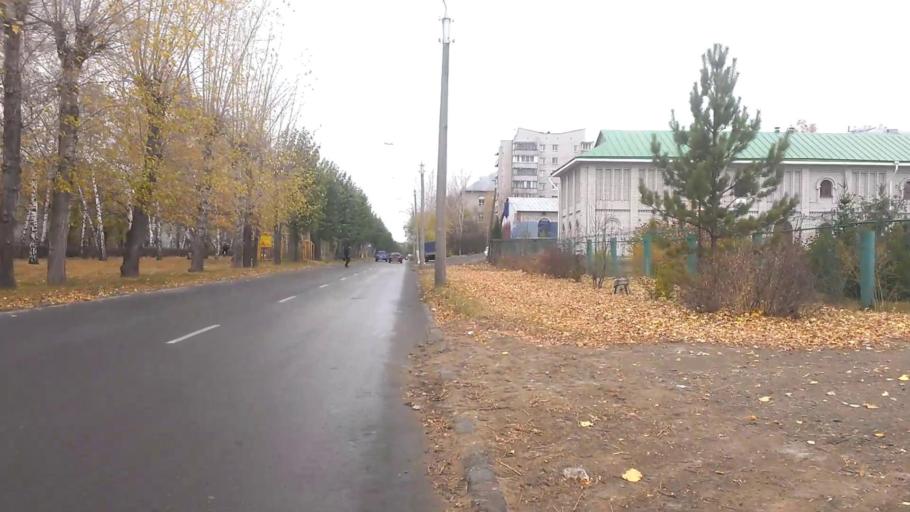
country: RU
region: Altai Krai
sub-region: Gorod Barnaulskiy
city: Barnaul
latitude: 53.3610
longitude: 83.7147
